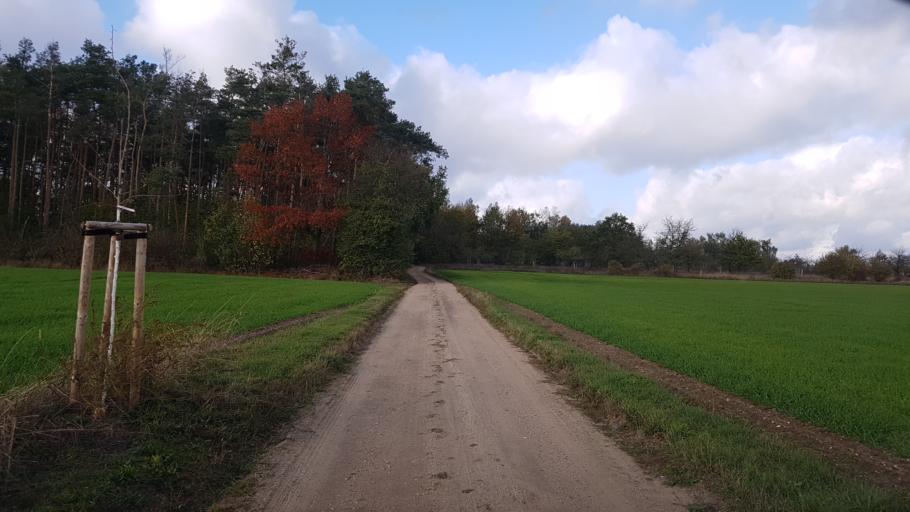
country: DE
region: Brandenburg
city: Doberlug-Kirchhain
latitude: 51.6329
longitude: 13.5357
